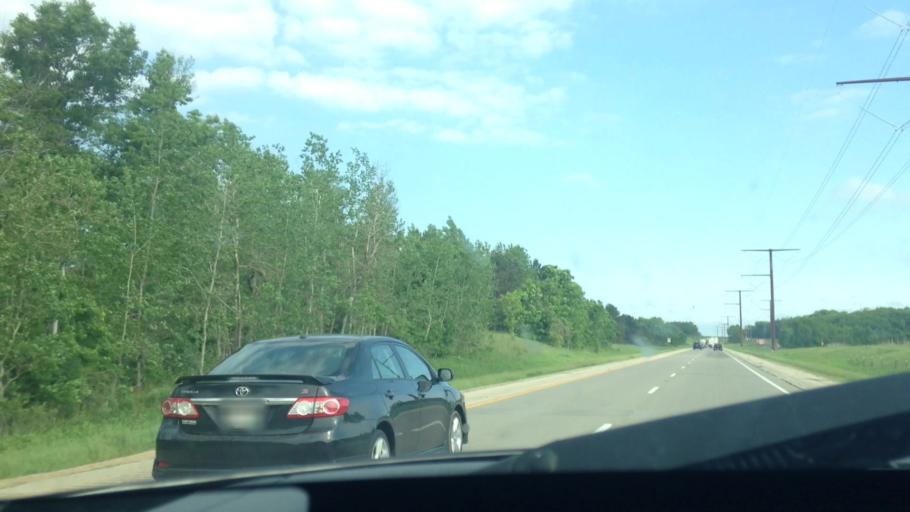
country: US
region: Wisconsin
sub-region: Juneau County
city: New Lisbon
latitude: 43.8554
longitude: -90.1086
